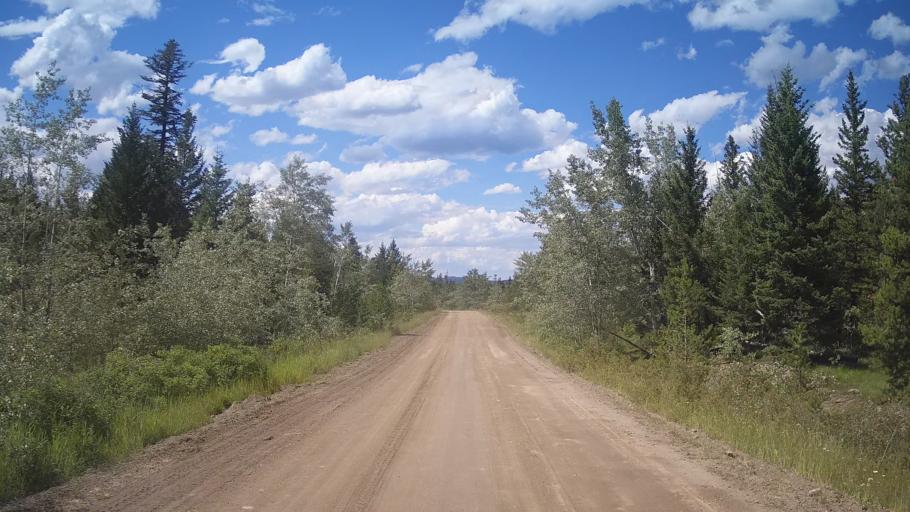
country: CA
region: British Columbia
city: Lillooet
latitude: 51.3370
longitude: -121.9089
